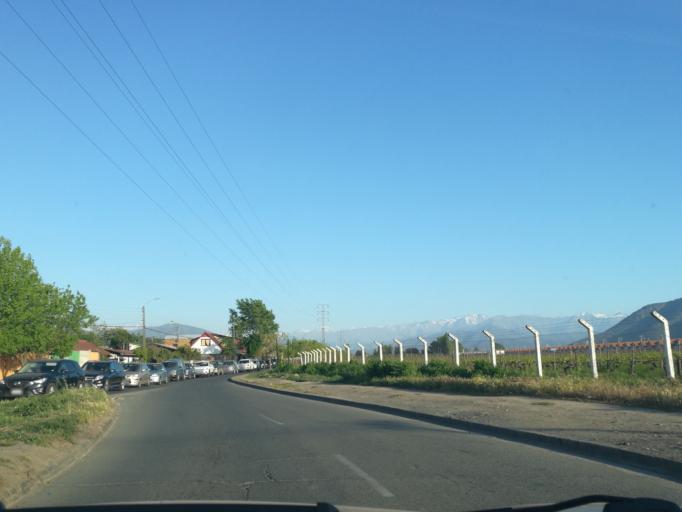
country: CL
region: O'Higgins
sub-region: Provincia de Cachapoal
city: Rancagua
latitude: -34.1847
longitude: -70.7398
